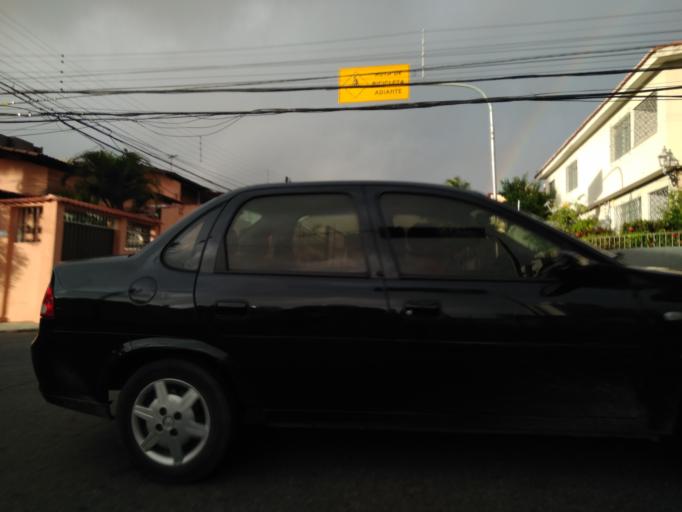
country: BR
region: Pernambuco
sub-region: Recife
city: Recife
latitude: -8.0348
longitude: -34.8892
